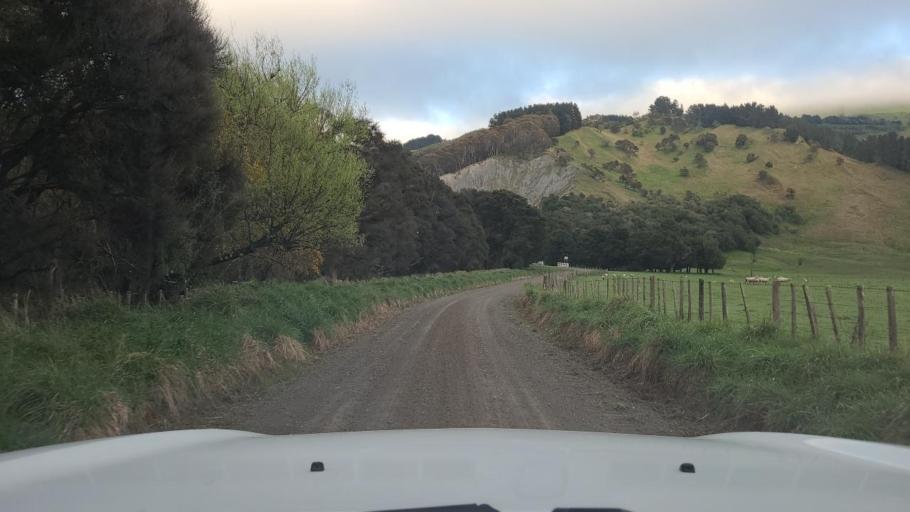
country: NZ
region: Wellington
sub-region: Masterton District
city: Masterton
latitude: -41.1779
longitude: 175.6884
